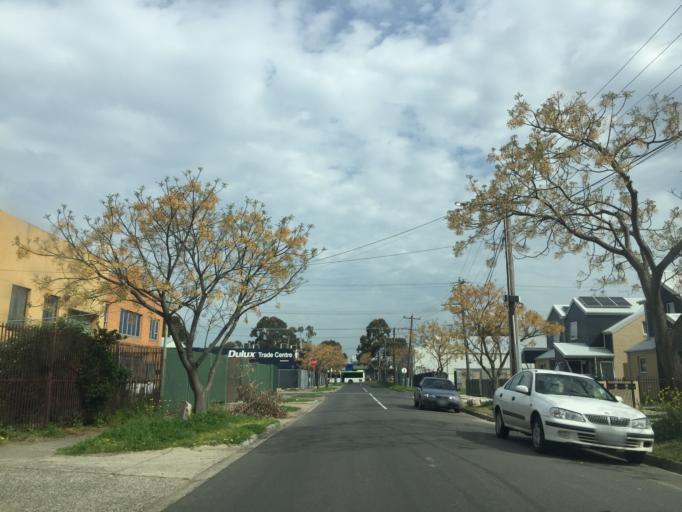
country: AU
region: Victoria
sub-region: Darebin
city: Preston
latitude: -37.7455
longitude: 145.0190
